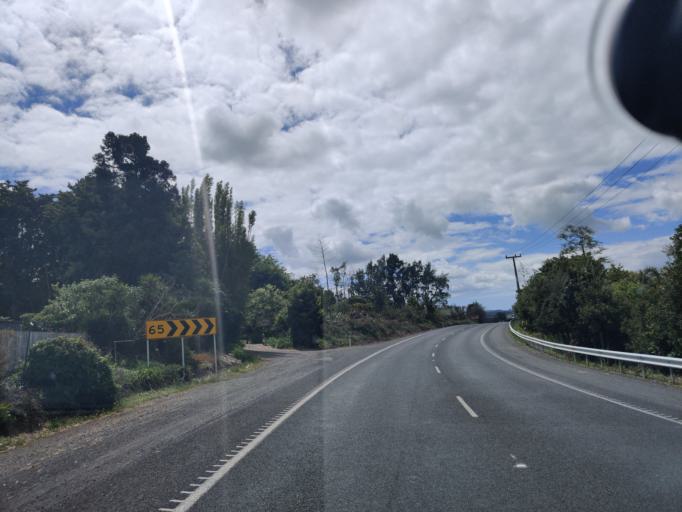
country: NZ
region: Northland
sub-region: Far North District
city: Kerikeri
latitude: -35.2403
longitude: 173.9193
